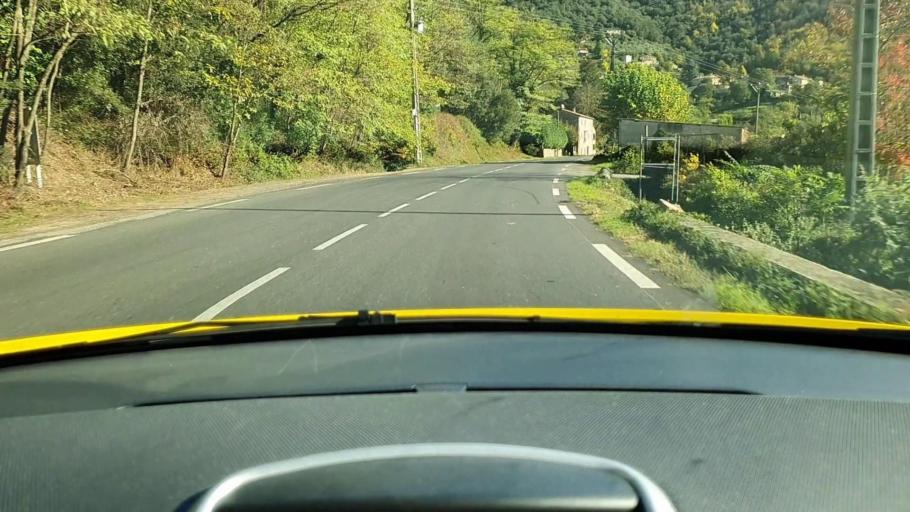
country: FR
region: Languedoc-Roussillon
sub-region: Departement du Gard
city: Sumene
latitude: 44.0230
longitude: 3.6828
